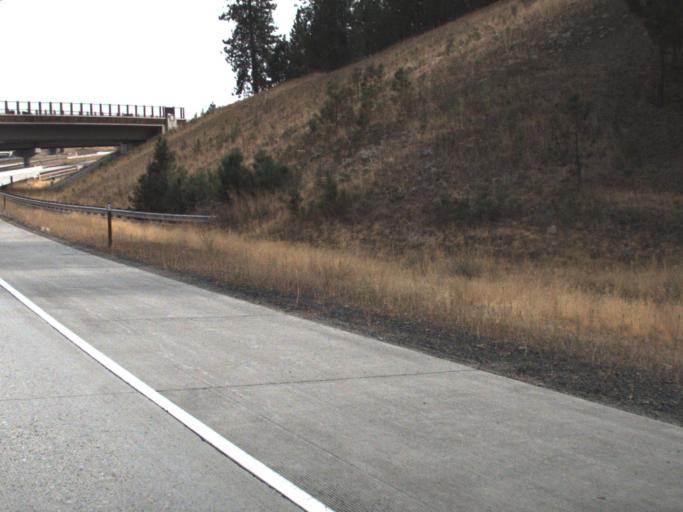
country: US
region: Washington
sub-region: Spokane County
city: Mead
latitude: 47.7771
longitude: -117.3759
